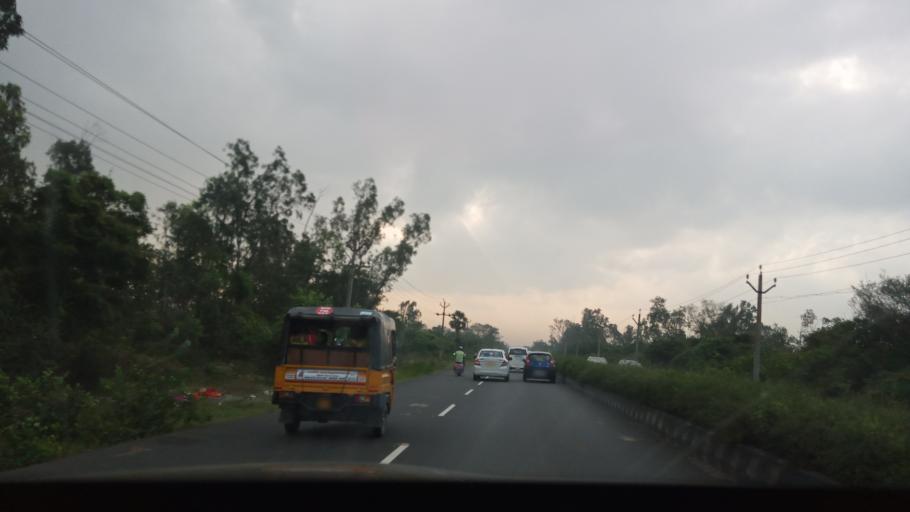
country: IN
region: Tamil Nadu
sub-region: Kancheepuram
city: Vengavasal
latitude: 12.8197
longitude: 80.1738
